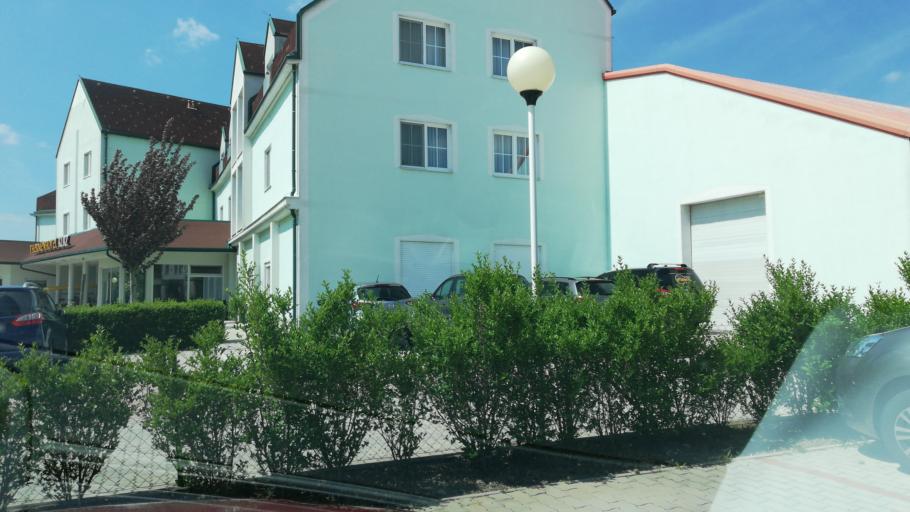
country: AT
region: Burgenland
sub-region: Politischer Bezirk Oberpullendorf
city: Lutzmannsburg
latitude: 47.4660
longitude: 16.6596
